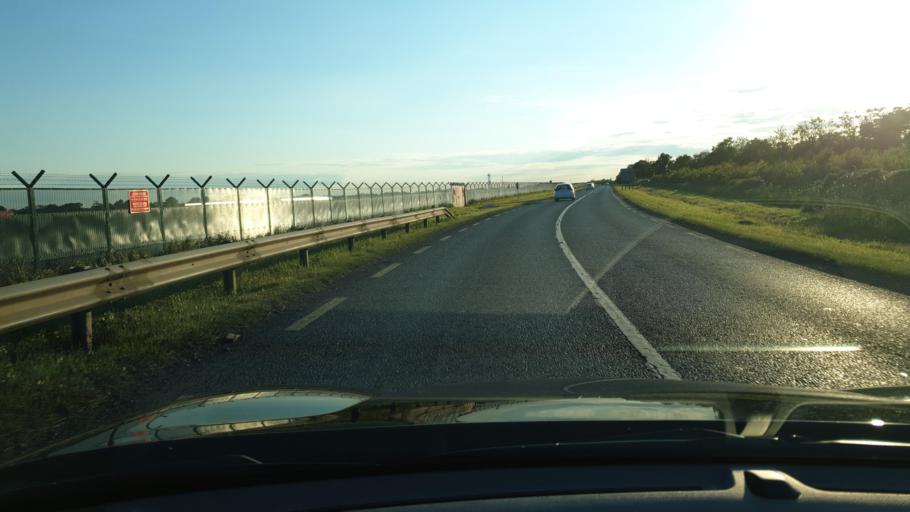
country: IE
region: Leinster
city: Ballymun
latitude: 53.4378
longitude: -6.2664
